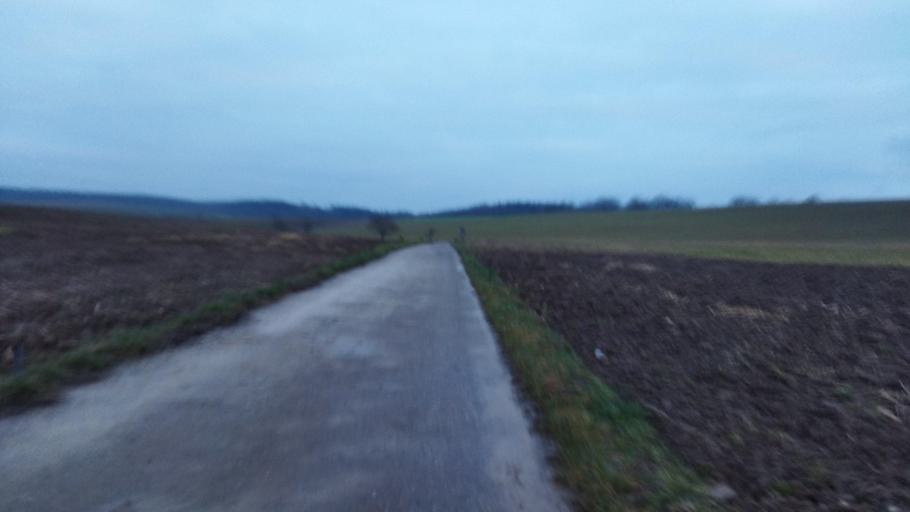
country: DE
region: Baden-Wuerttemberg
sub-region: Regierungsbezirk Stuttgart
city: Bad Rappenau
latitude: 49.2050
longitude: 9.0941
